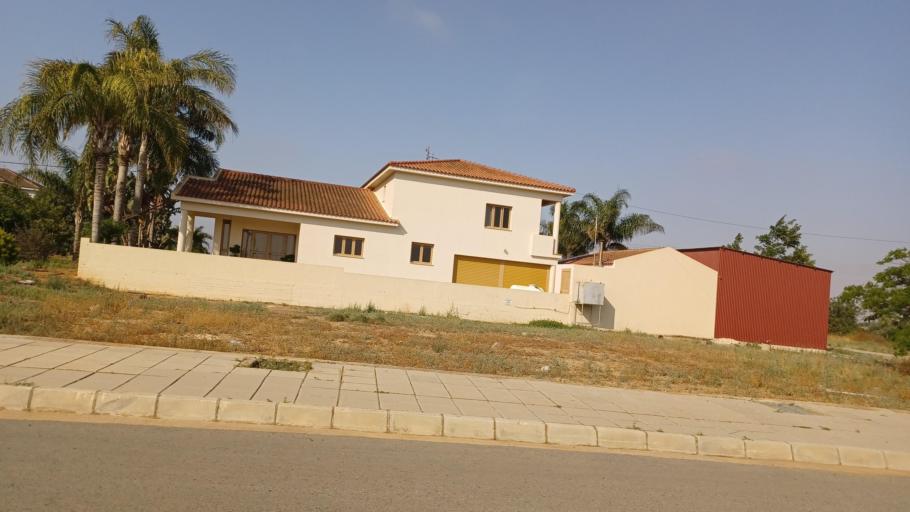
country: CY
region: Ammochostos
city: Avgorou
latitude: 35.0419
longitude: 33.8333
